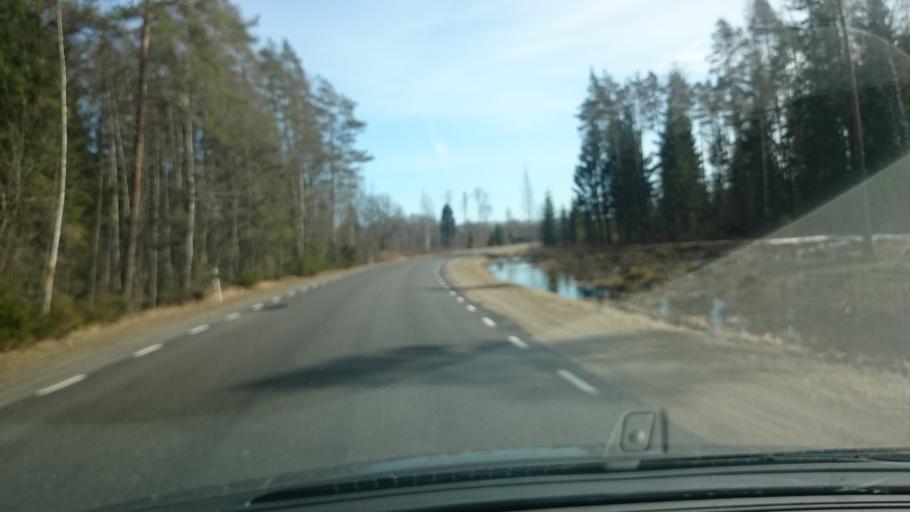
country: EE
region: Paernumaa
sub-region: Tootsi vald
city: Tootsi
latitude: 58.6409
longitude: 24.9014
